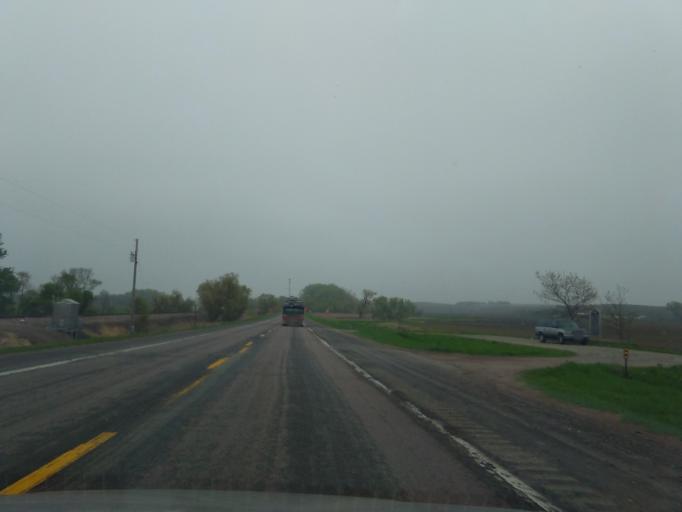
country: US
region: Nebraska
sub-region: Burt County
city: Oakland
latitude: 41.8028
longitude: -96.4809
